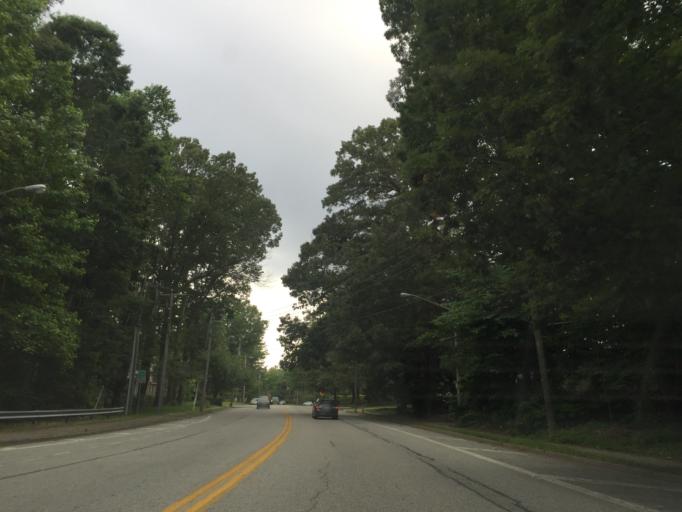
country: US
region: Virginia
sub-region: York County
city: Yorktown
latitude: 37.1022
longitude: -76.5229
